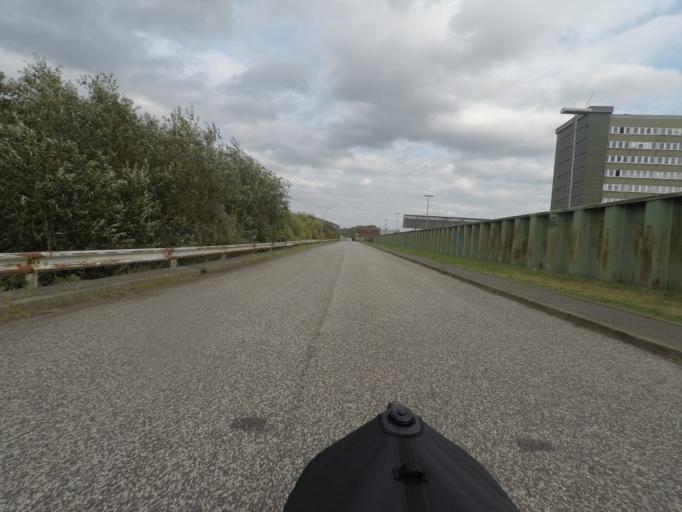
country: DE
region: Hamburg
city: Hamburg-Mitte
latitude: 53.5334
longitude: 10.0159
